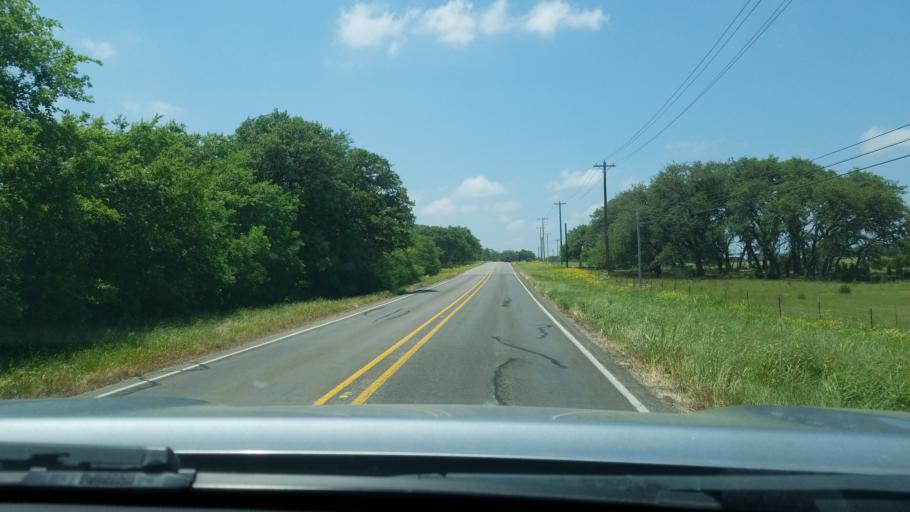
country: US
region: Texas
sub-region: Hays County
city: Woodcreek
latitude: 30.0232
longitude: -98.1594
